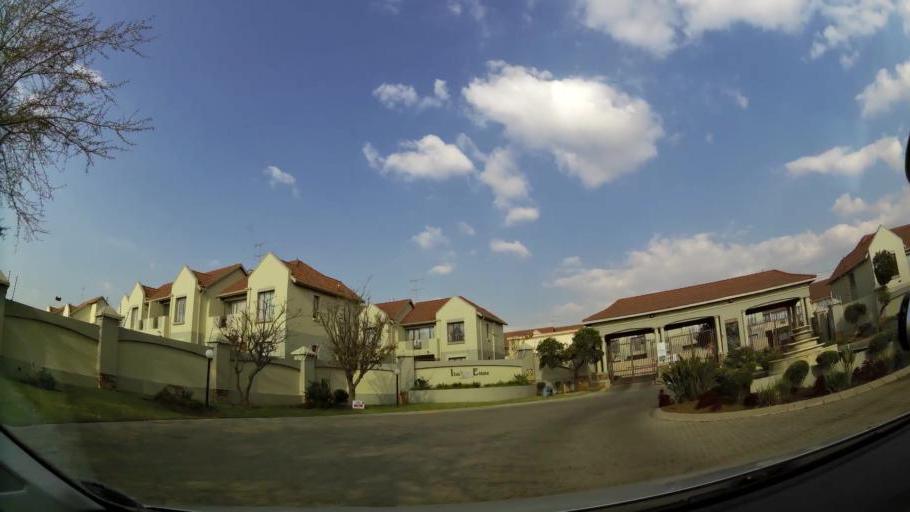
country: ZA
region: Gauteng
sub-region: City of Johannesburg Metropolitan Municipality
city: Modderfontein
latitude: -26.1065
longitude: 28.1892
